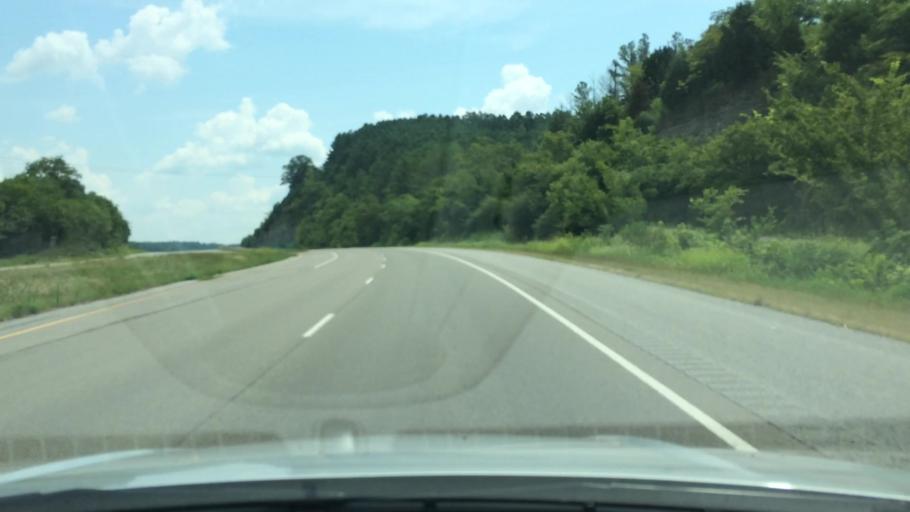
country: US
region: Tennessee
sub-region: Giles County
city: Pulaski
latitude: 35.1751
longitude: -86.9923
